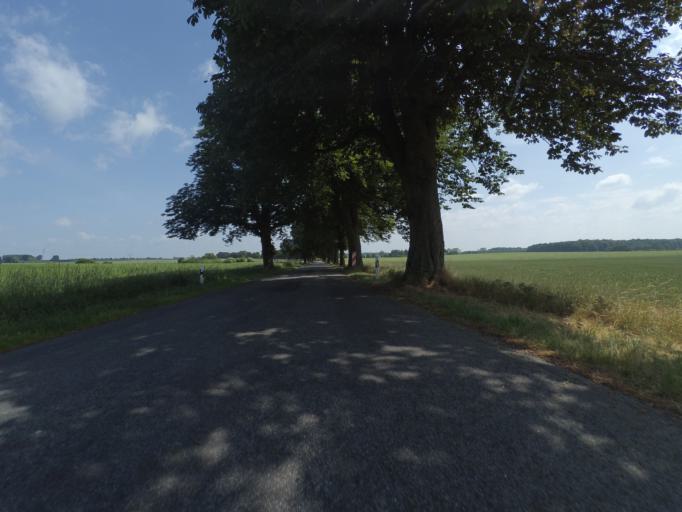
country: DE
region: Mecklenburg-Vorpommern
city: Lubz
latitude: 53.4475
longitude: 12.0630
